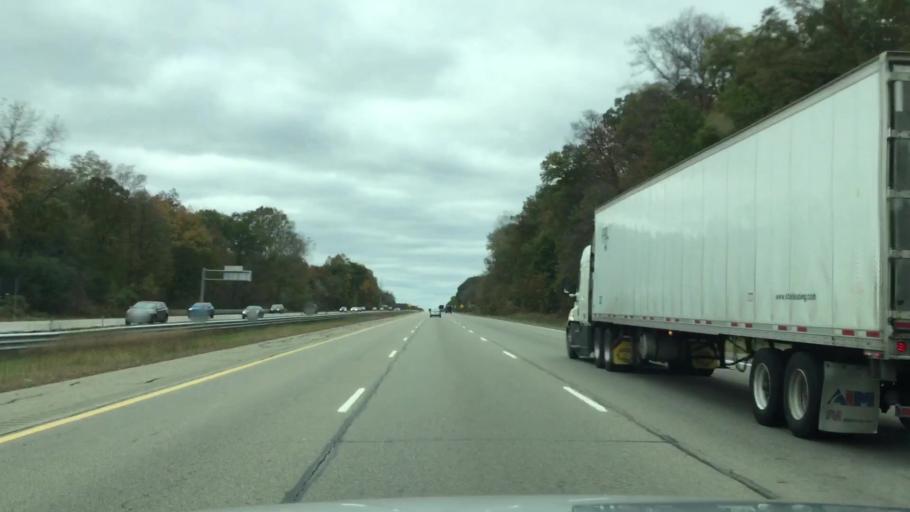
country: US
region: Michigan
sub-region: Washtenaw County
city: Dexter
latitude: 42.2985
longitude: -83.8808
